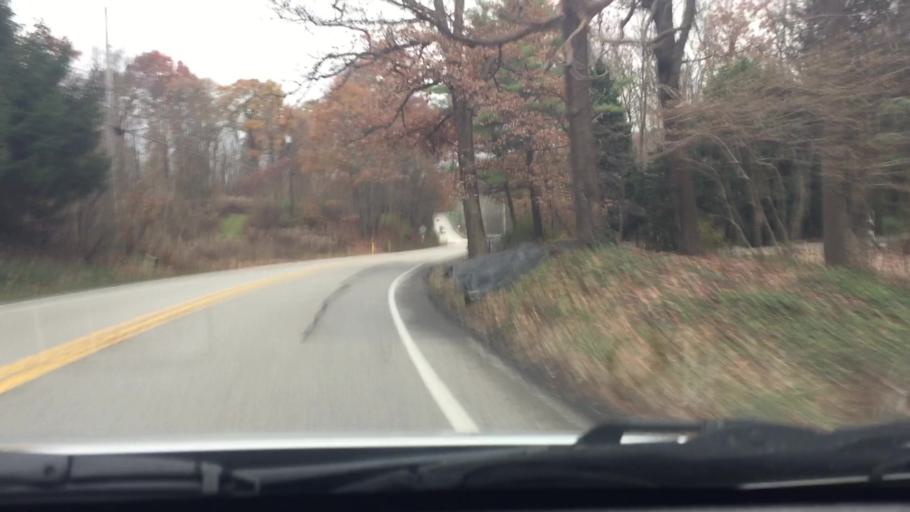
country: US
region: Pennsylvania
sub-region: Butler County
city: Nixon
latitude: 40.7211
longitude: -79.8820
